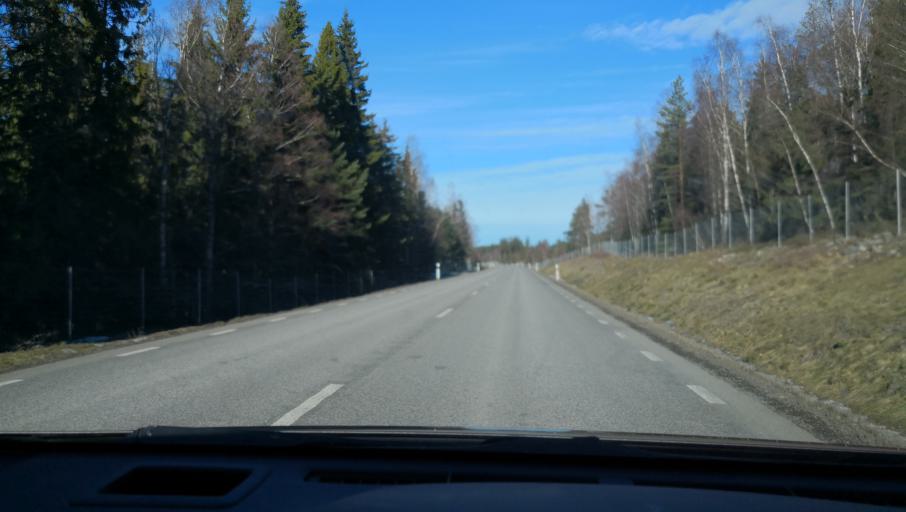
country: SE
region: Uppsala
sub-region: Uppsala Kommun
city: Vattholma
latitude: 60.0385
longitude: 17.7505
